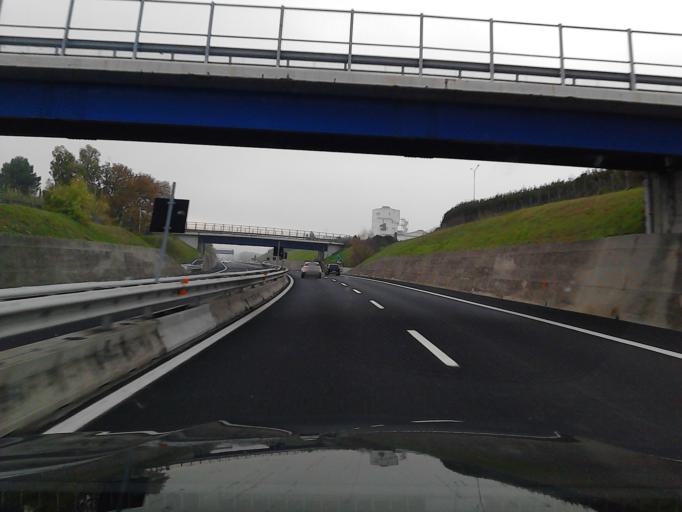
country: IT
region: Abruzzo
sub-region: Provincia di Pescara
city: San Martino Bassa
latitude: 42.5055
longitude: 14.1186
